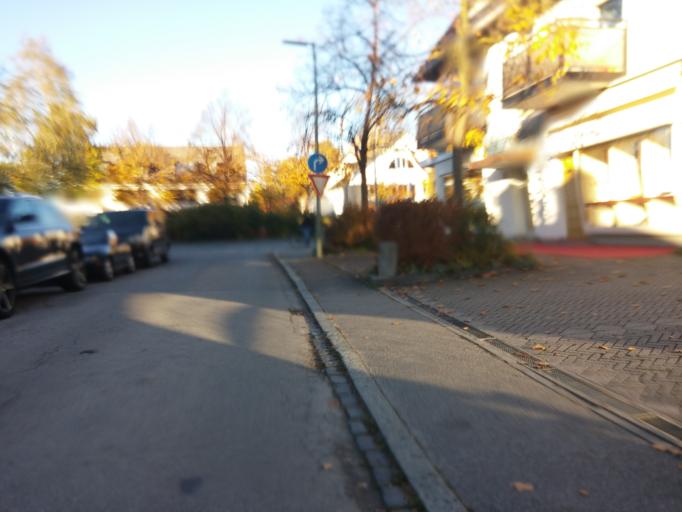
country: DE
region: Bavaria
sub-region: Upper Bavaria
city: Haar
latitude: 48.1123
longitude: 11.7034
